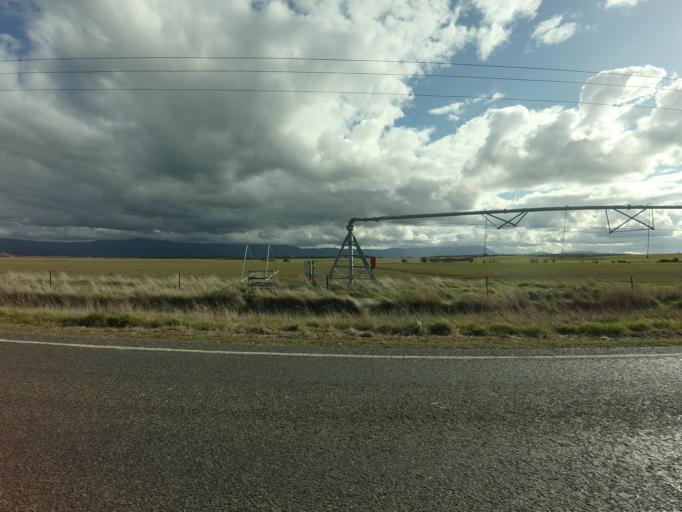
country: AU
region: Tasmania
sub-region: Northern Midlands
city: Longford
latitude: -41.7061
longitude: 147.0788
